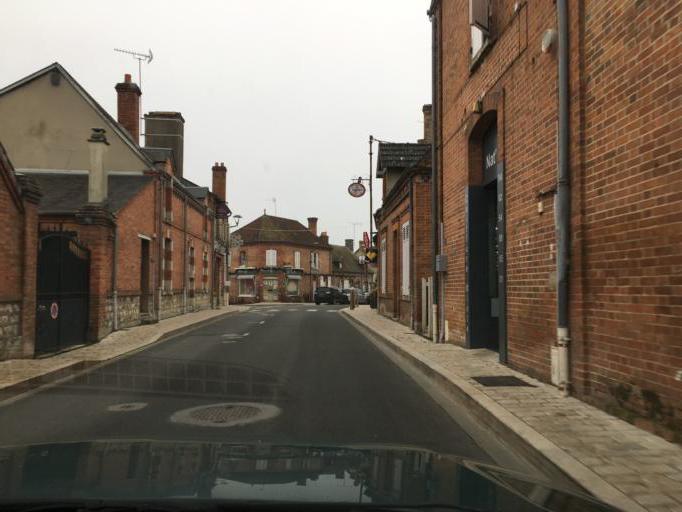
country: FR
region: Centre
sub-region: Departement du Loir-et-Cher
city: Chaumont-sur-Tharonne
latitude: 47.6325
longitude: 1.8527
